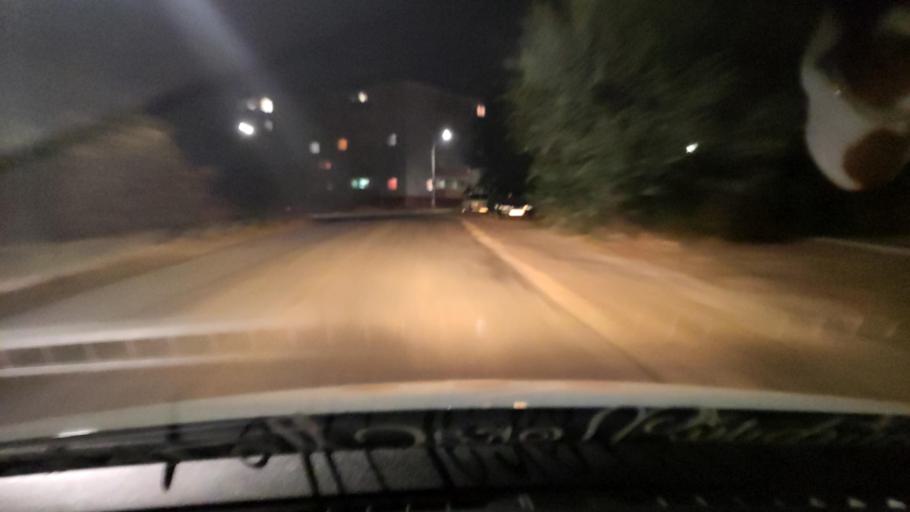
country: RU
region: Voronezj
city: Semiluki
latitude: 51.6897
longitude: 39.0165
